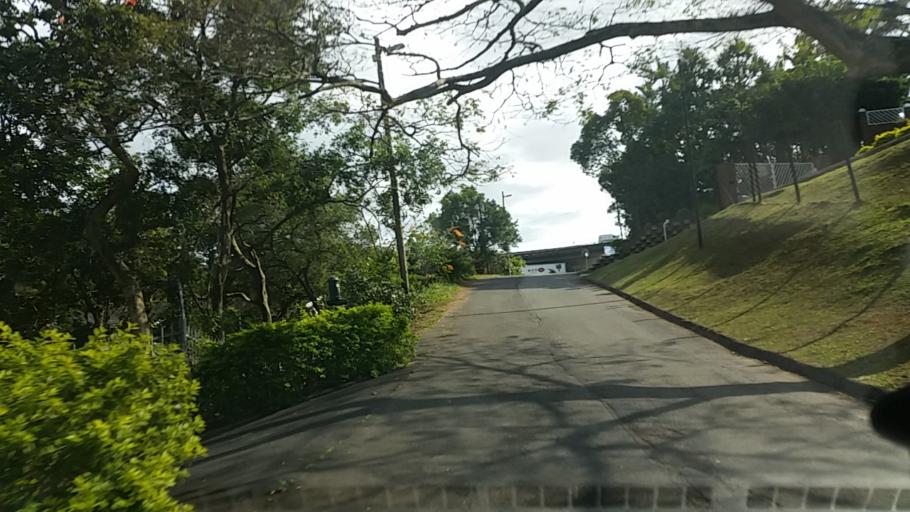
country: ZA
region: KwaZulu-Natal
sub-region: eThekwini Metropolitan Municipality
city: Berea
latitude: -29.8302
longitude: 30.9584
